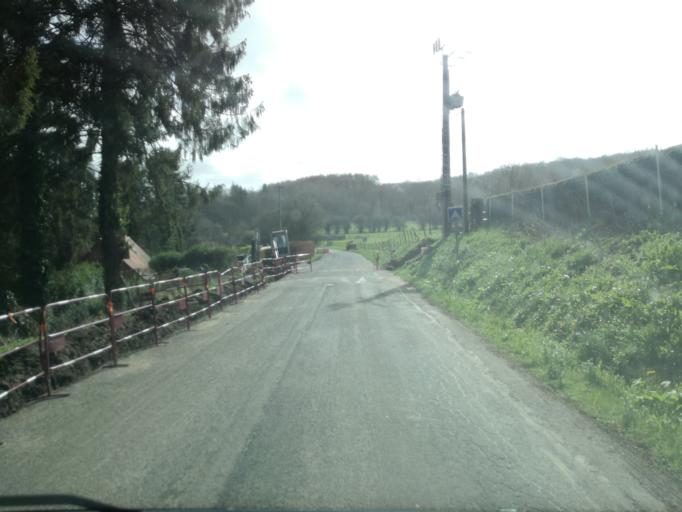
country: FR
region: Haute-Normandie
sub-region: Departement de la Seine-Maritime
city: Bretteville-du-Grand-Caux
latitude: 49.7020
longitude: 0.4514
